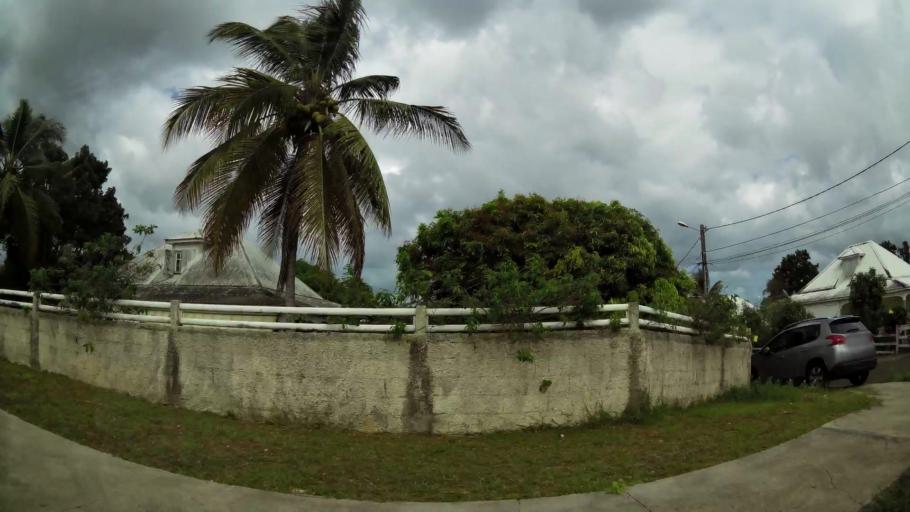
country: GP
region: Guadeloupe
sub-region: Guadeloupe
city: Baie-Mahault
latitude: 16.2568
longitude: -61.5797
